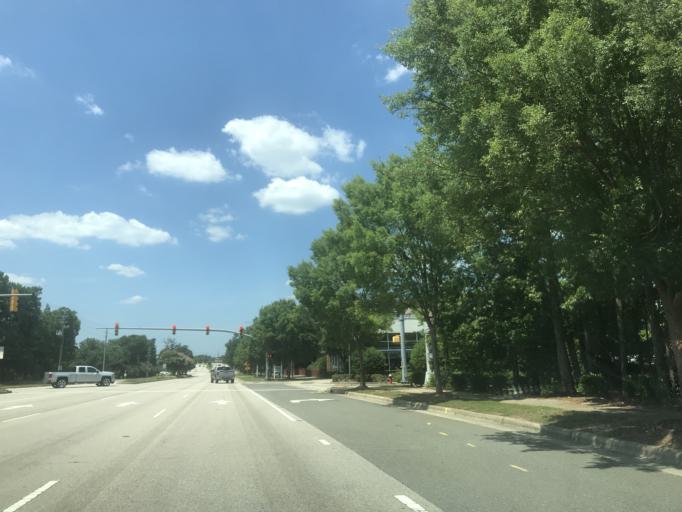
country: US
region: North Carolina
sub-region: Wake County
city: Cary
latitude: 35.7526
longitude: -78.7411
